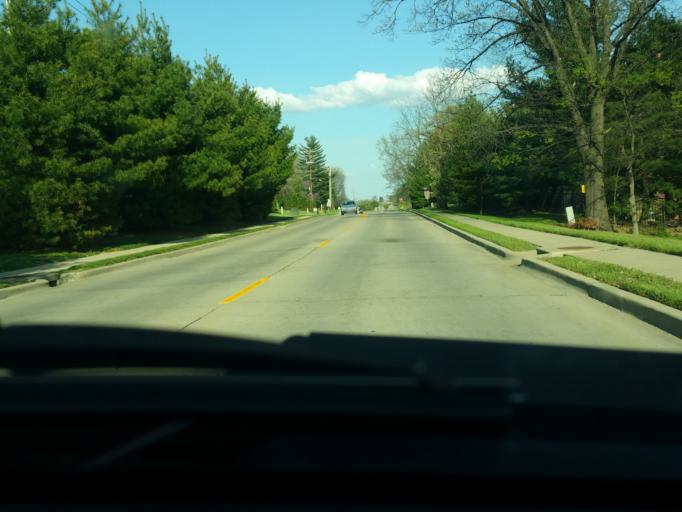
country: US
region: Illinois
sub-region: Madison County
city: Edwardsville
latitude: 38.7813
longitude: -89.9412
